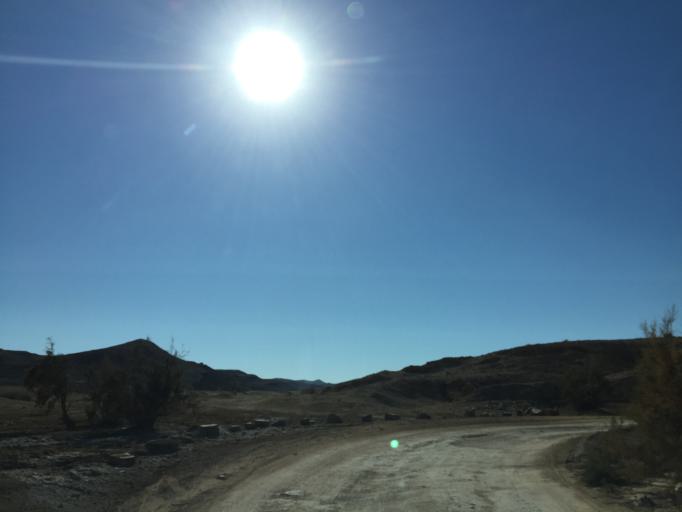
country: IL
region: Southern District
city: Mitzpe Ramon
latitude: 30.6128
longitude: 34.9108
